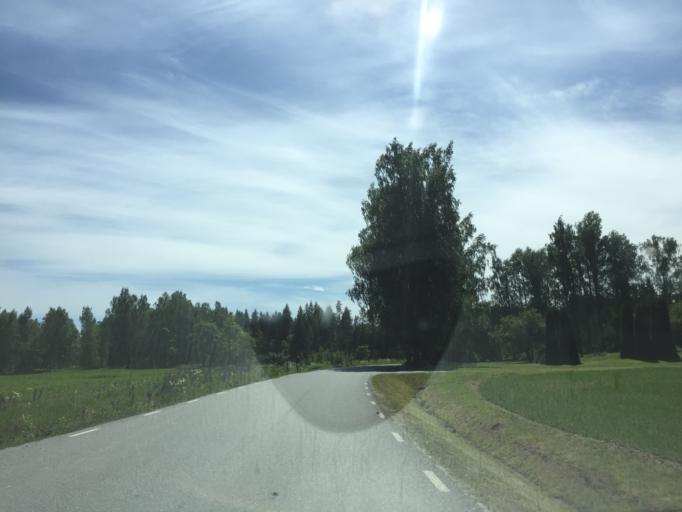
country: SE
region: OErebro
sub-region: Orebro Kommun
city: Hovsta
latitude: 59.3835
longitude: 15.1753
